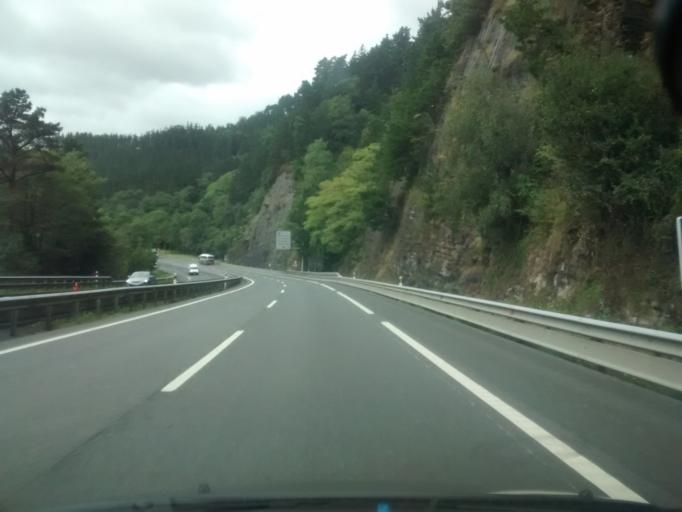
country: ES
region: Basque Country
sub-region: Provincia de Guipuzcoa
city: Elgoibar
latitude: 43.2360
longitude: -2.4027
